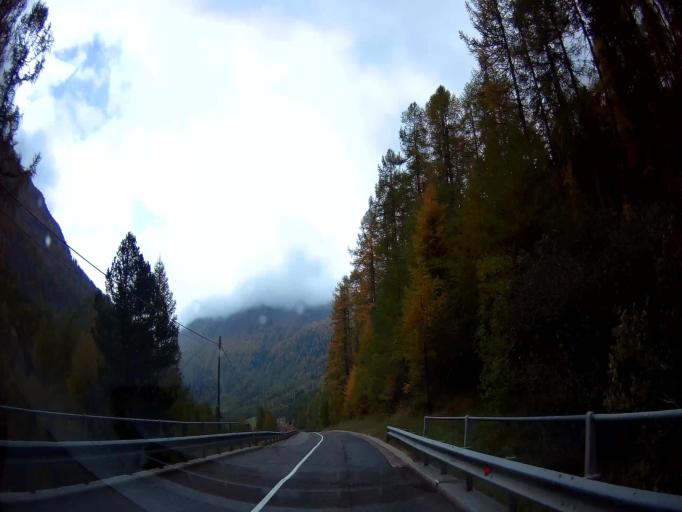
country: IT
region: Trentino-Alto Adige
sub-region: Bolzano
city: Silandro
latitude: 46.7390
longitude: 10.7932
